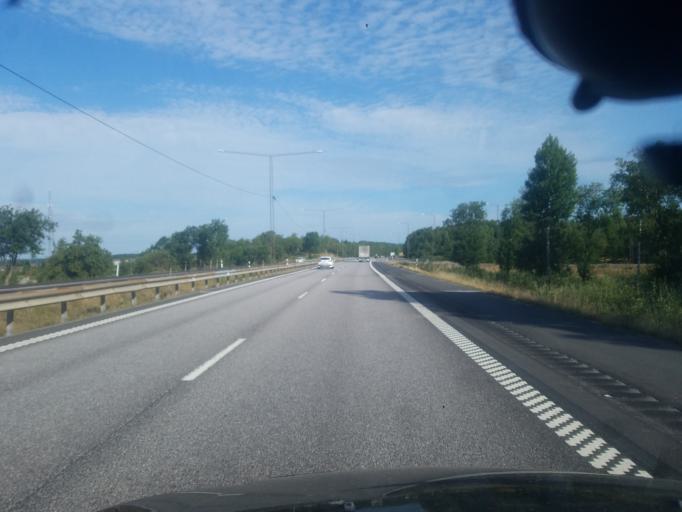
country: SE
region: Vaestra Goetaland
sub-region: Kungalvs Kommun
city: Kode
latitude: 57.9438
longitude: 11.8580
